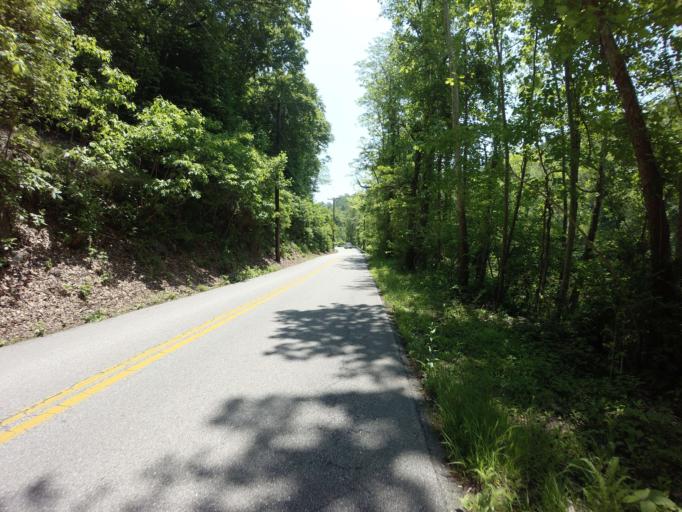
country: US
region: Maryland
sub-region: Howard County
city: Ilchester
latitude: 39.2541
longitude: -76.7697
